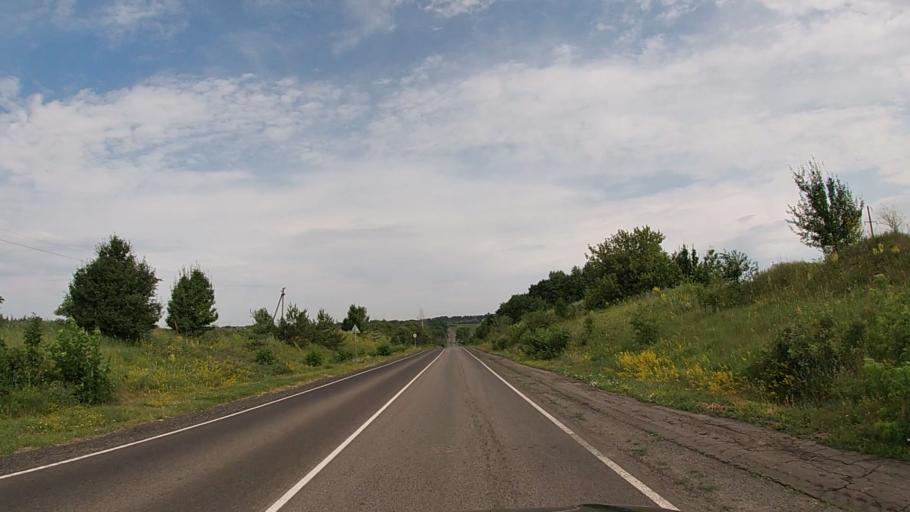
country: RU
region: Belgorod
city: Krasnaya Yaruga
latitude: 50.8231
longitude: 35.5006
